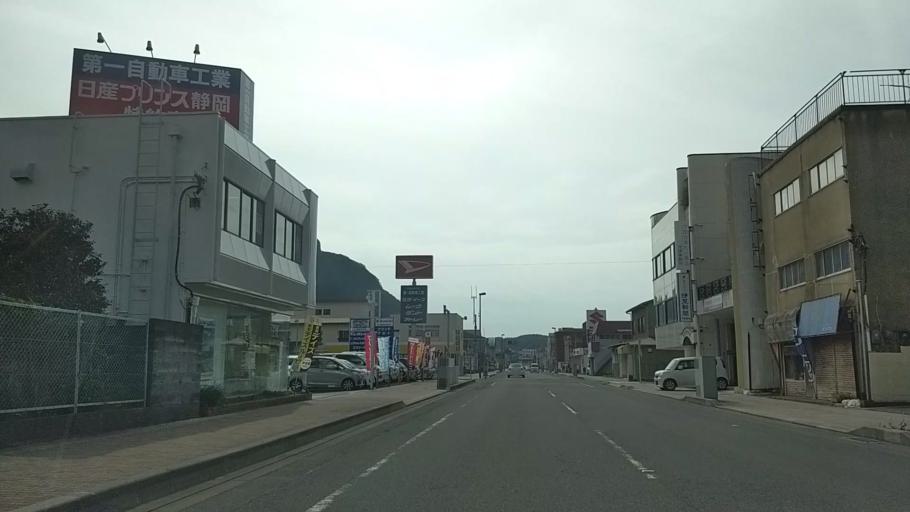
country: JP
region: Shizuoka
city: Shimoda
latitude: 34.6851
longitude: 138.9455
